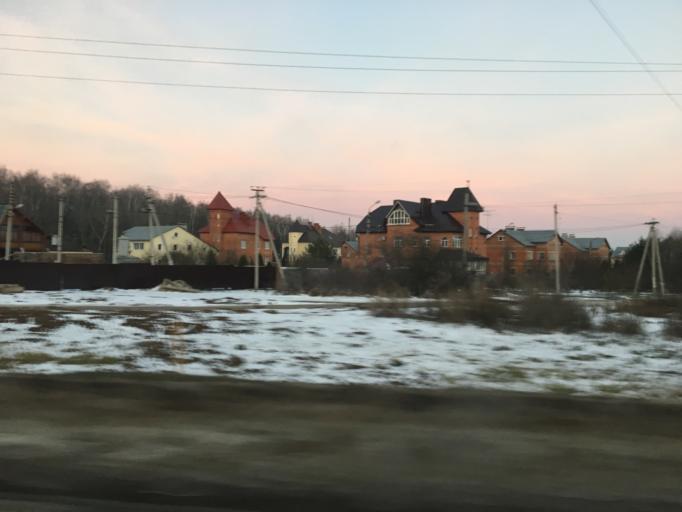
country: RU
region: Tula
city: Gorelki
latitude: 54.2496
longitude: 37.6123
